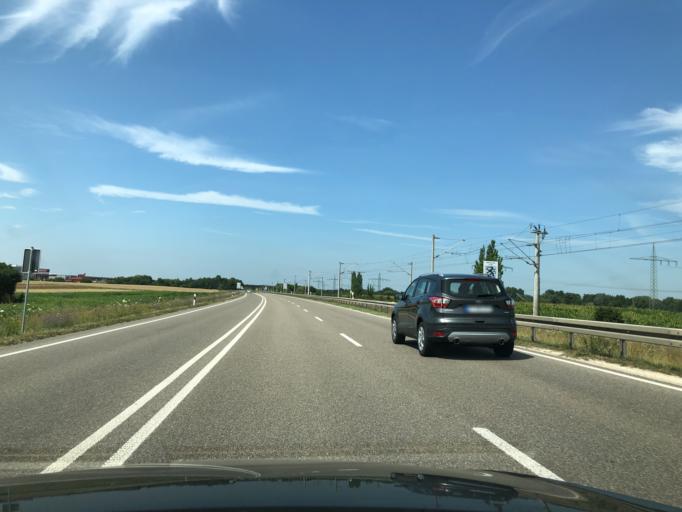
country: DE
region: Bavaria
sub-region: Upper Bavaria
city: Karlskron
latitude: 48.7100
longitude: 11.4342
